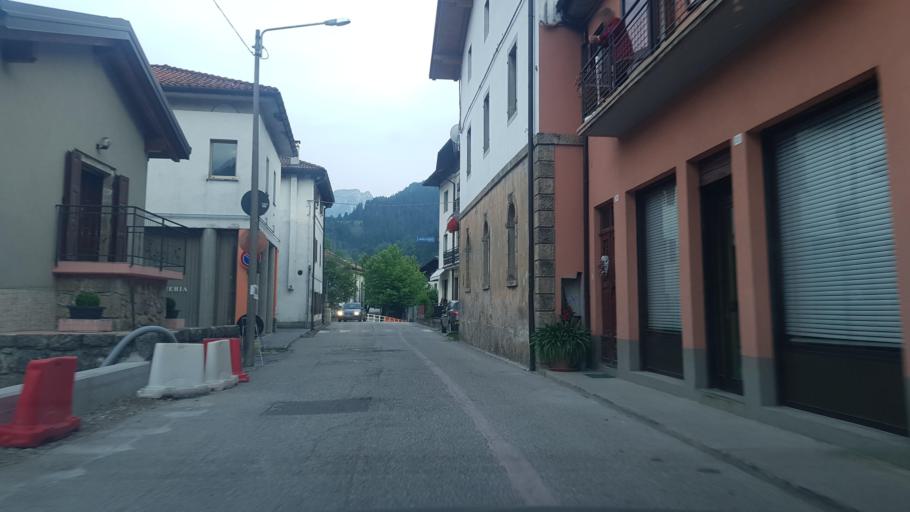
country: IT
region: Friuli Venezia Giulia
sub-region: Provincia di Udine
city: Paularo
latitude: 46.5324
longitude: 13.1157
